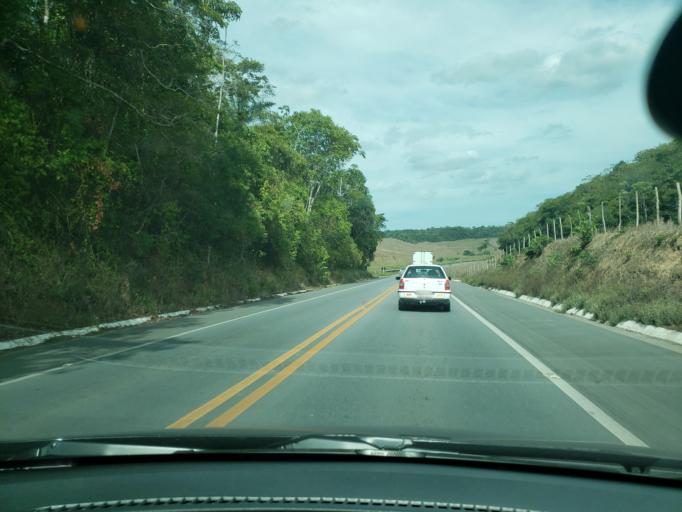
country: BR
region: Alagoas
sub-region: Murici
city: Murici
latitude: -9.3307
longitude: -35.9090
